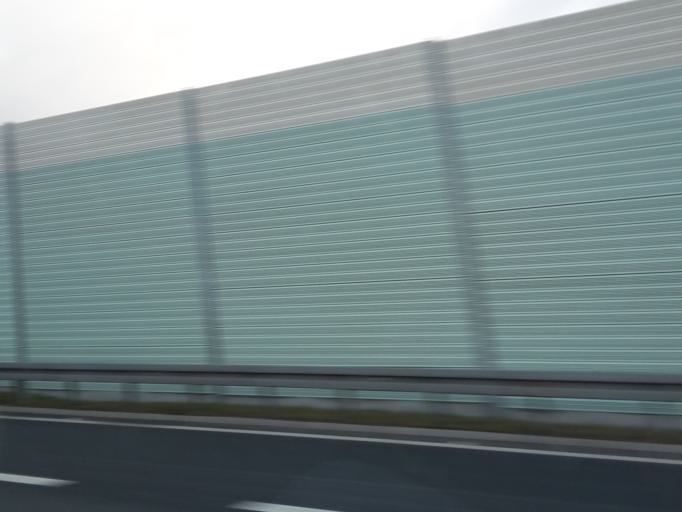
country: PL
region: Warmian-Masurian Voivodeship
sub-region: Powiat ostrodzki
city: Maldyty
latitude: 53.9727
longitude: 19.6974
